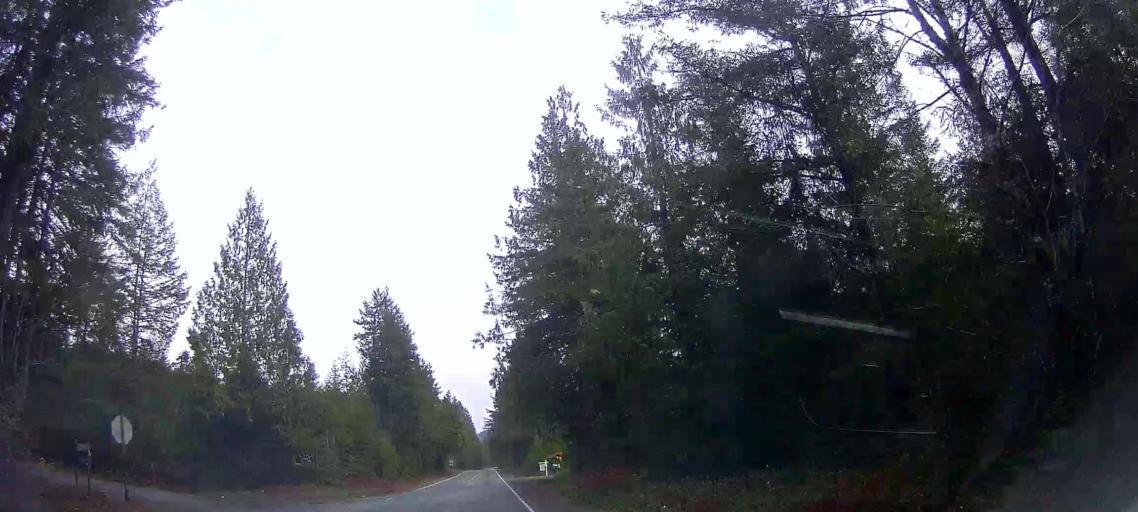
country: US
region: Washington
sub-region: Snohomish County
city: Darrington
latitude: 48.5279
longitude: -121.8262
